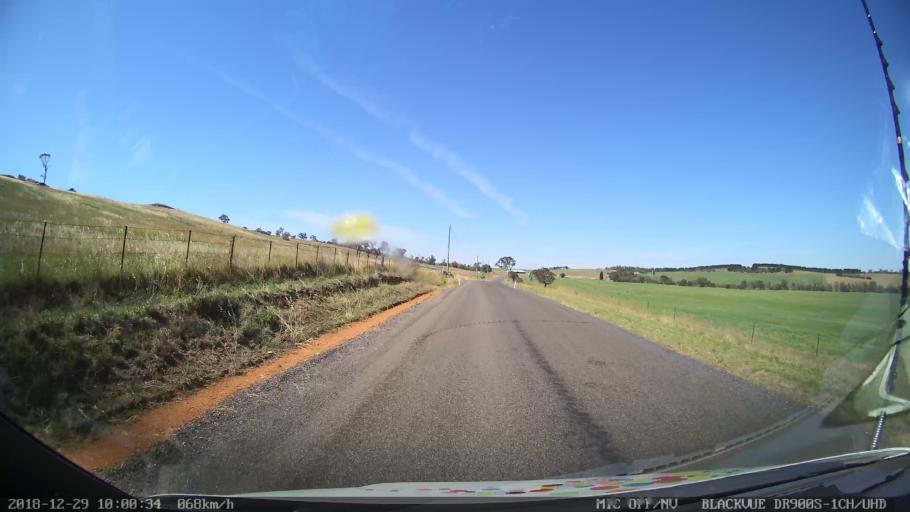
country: AU
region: New South Wales
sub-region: Goulburn Mulwaree
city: Goulburn
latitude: -34.7932
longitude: 149.4847
